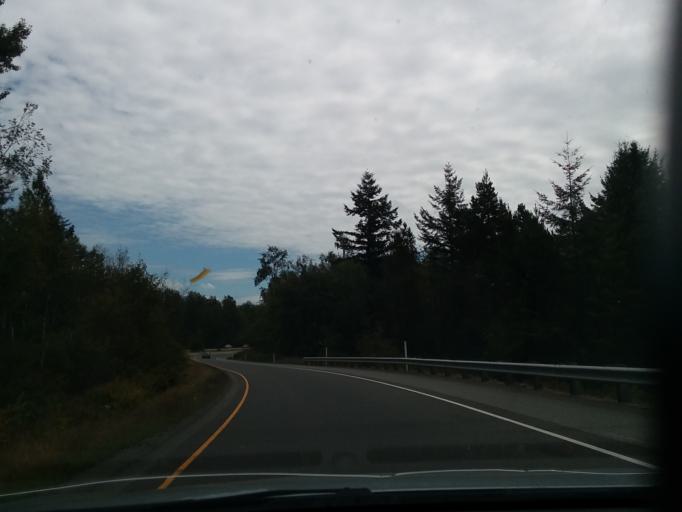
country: US
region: Washington
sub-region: Whatcom County
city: Birch Bay
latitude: 48.9345
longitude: -122.6623
